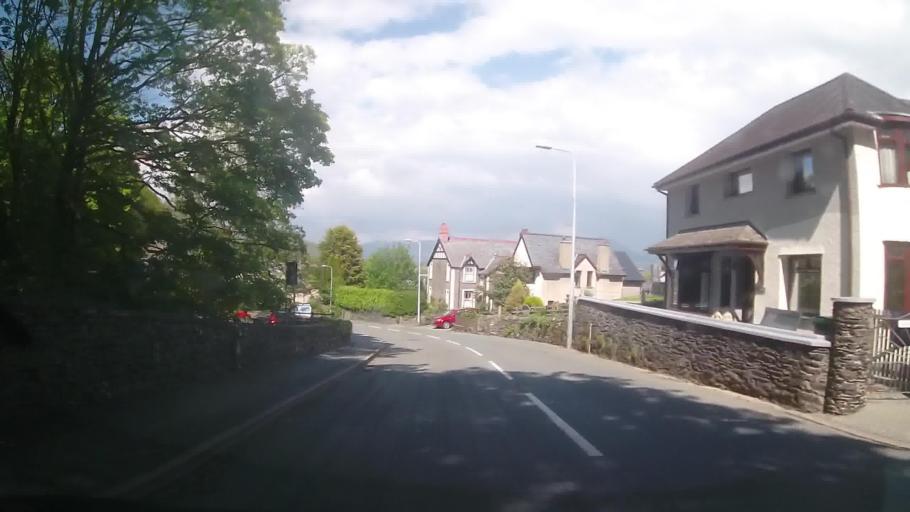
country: GB
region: Wales
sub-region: Gwynedd
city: Porthmadog
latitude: 52.9239
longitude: -4.1337
